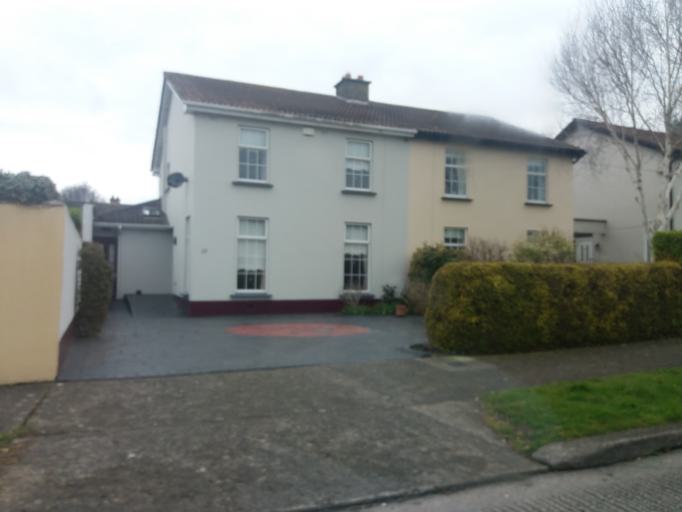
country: IE
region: Leinster
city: Portmarnock
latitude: 53.4363
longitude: -6.1334
